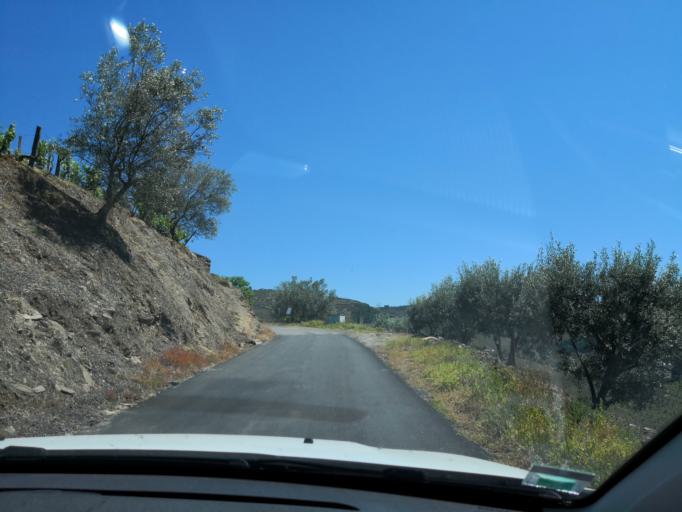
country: PT
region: Vila Real
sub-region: Vila Real
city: Vila Real
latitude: 41.2292
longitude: -7.7224
